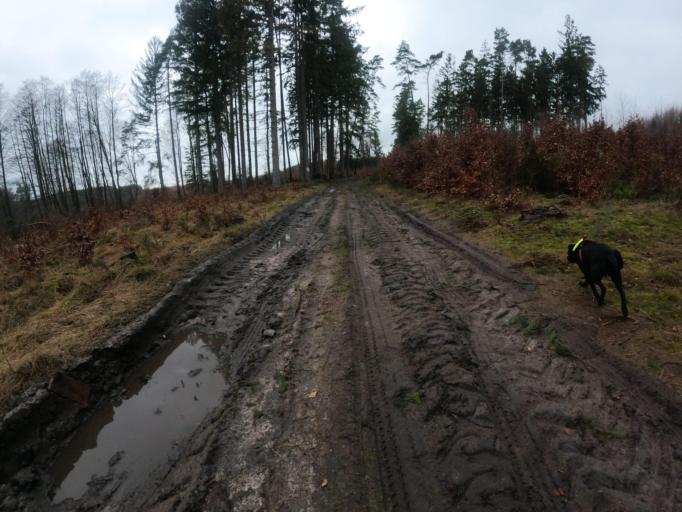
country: PL
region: West Pomeranian Voivodeship
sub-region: Powiat koszalinski
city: Polanow
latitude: 54.2400
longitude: 16.6934
